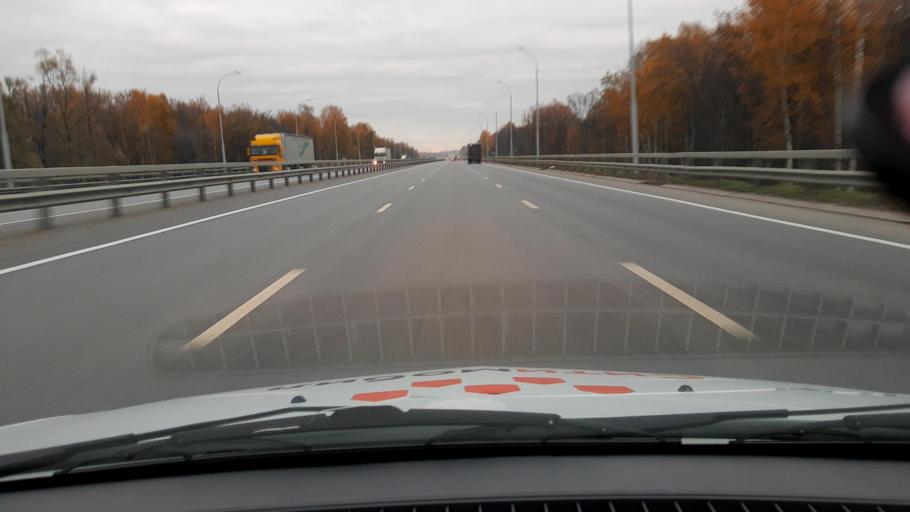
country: RU
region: Bashkortostan
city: Ufa
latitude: 54.6479
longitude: 56.0385
